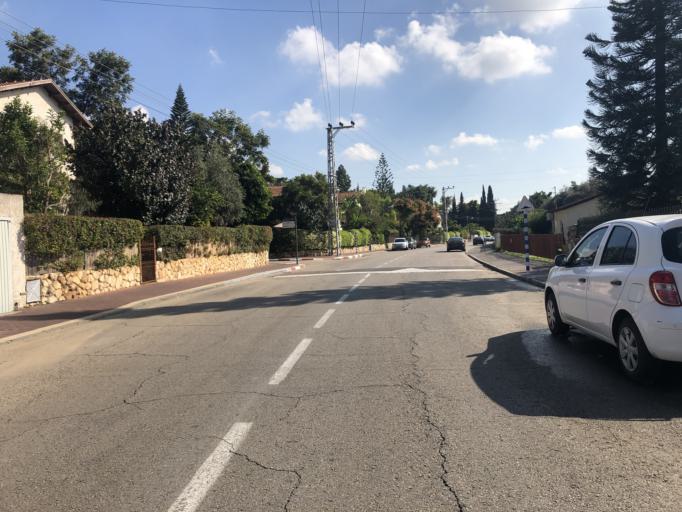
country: IL
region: Tel Aviv
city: Or Yehuda
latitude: 32.0324
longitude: 34.8720
